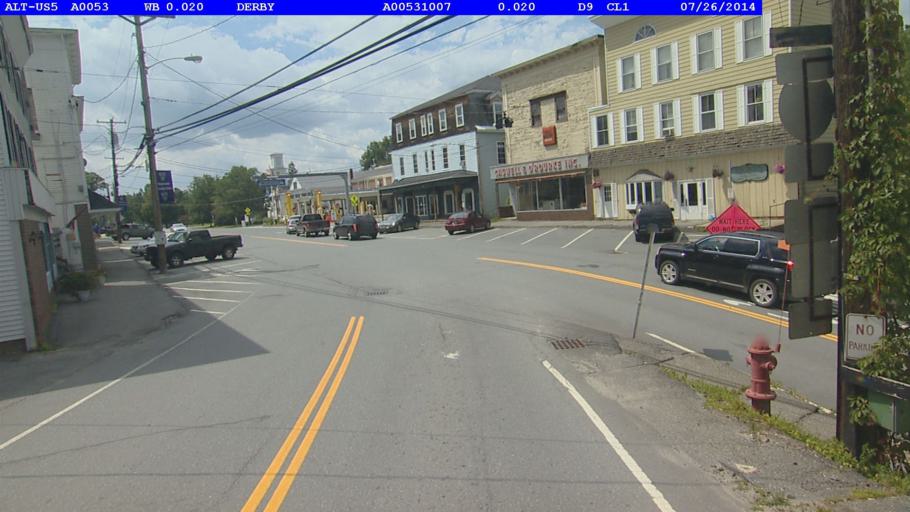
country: US
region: Vermont
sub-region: Orleans County
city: Newport
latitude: 45.0053
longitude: -72.0995
